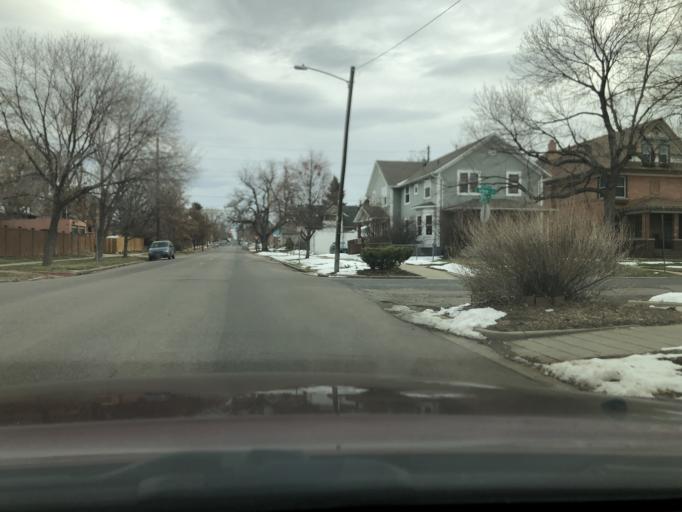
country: US
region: Colorado
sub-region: Denver County
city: Denver
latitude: 39.7582
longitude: -104.9625
